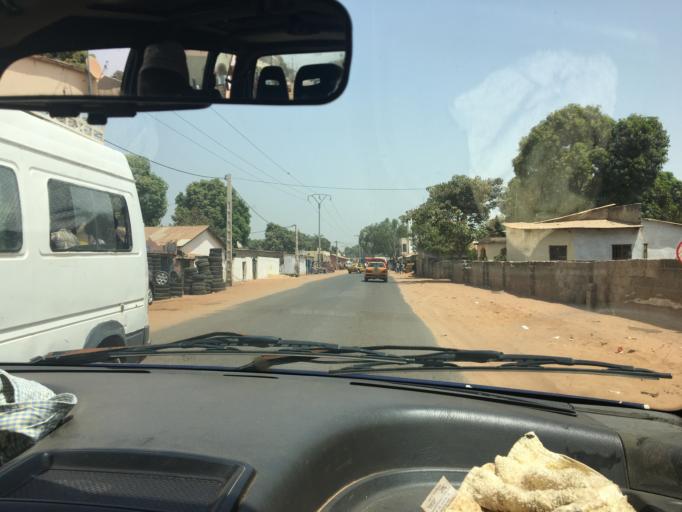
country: GM
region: Western
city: Abuko
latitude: 13.3952
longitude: -16.6737
